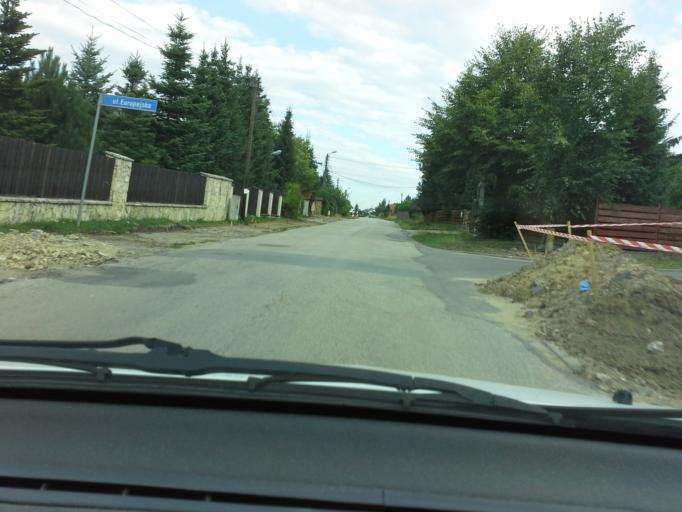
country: PL
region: Lesser Poland Voivodeship
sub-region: Powiat chrzanowski
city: Trzebinia
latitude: 50.1333
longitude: 19.4477
